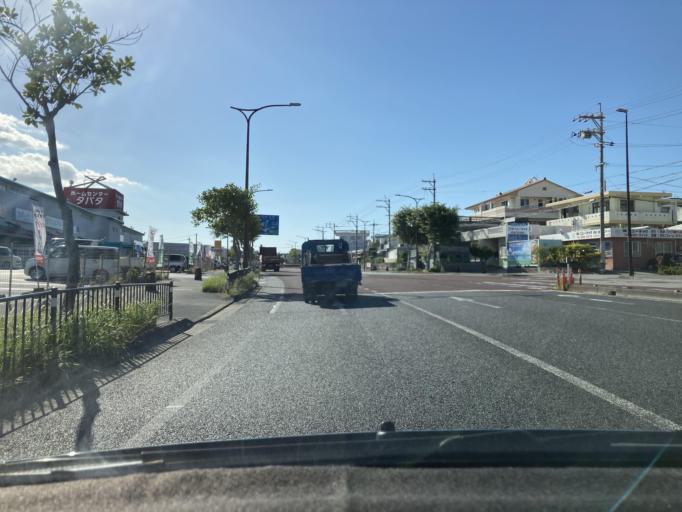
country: JP
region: Okinawa
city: Ishikawa
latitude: 26.4346
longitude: 127.8356
